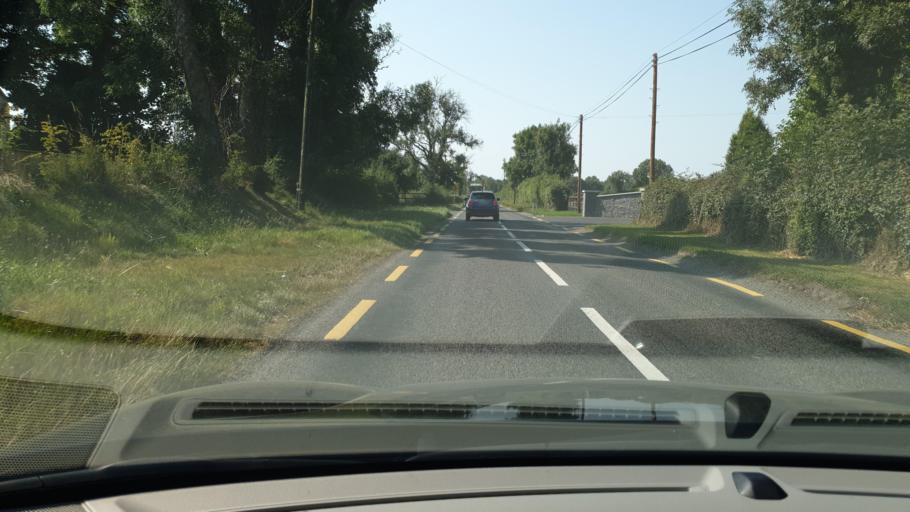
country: IE
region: Leinster
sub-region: An Mhi
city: Trim
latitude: 53.5776
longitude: -6.8360
